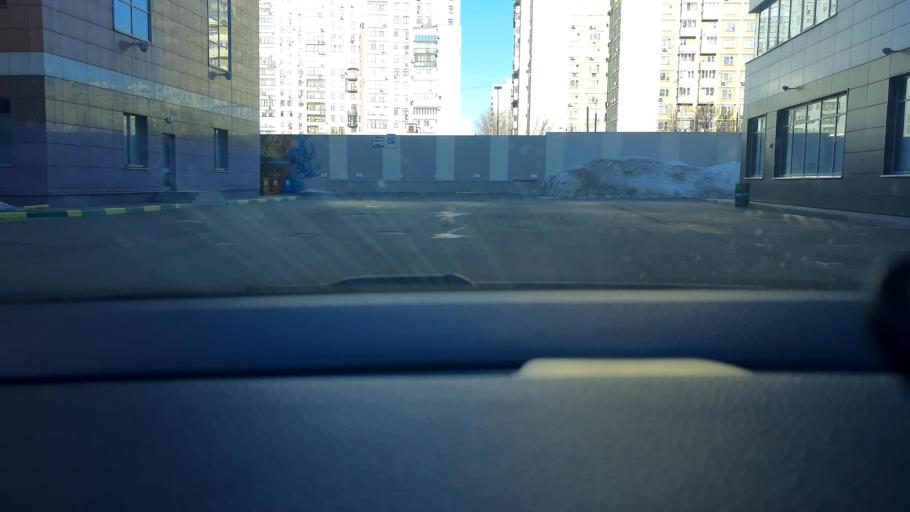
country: RU
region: Moscow
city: Otradnoye
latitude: 55.8567
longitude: 37.5997
